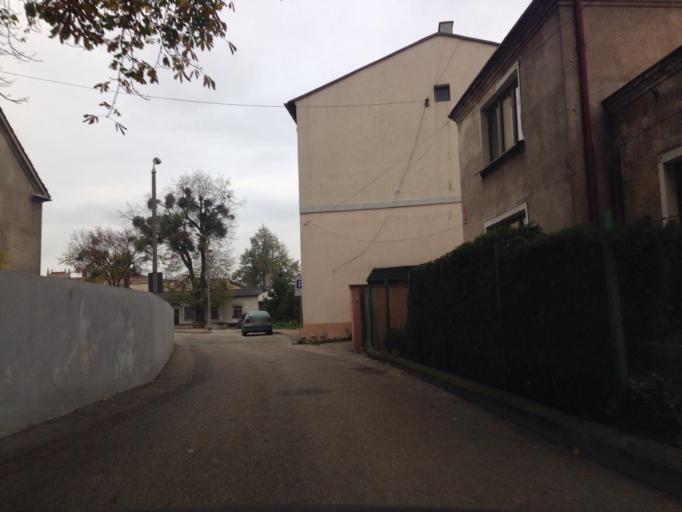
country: PL
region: Kujawsko-Pomorskie
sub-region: Powiat brodnicki
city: Brodnica
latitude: 53.2568
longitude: 19.4049
